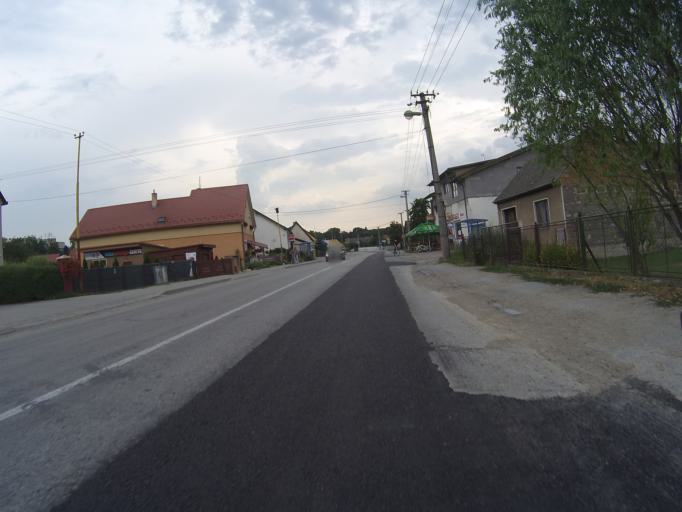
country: SK
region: Nitriansky
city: Ilava
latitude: 49.0388
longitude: 18.2888
